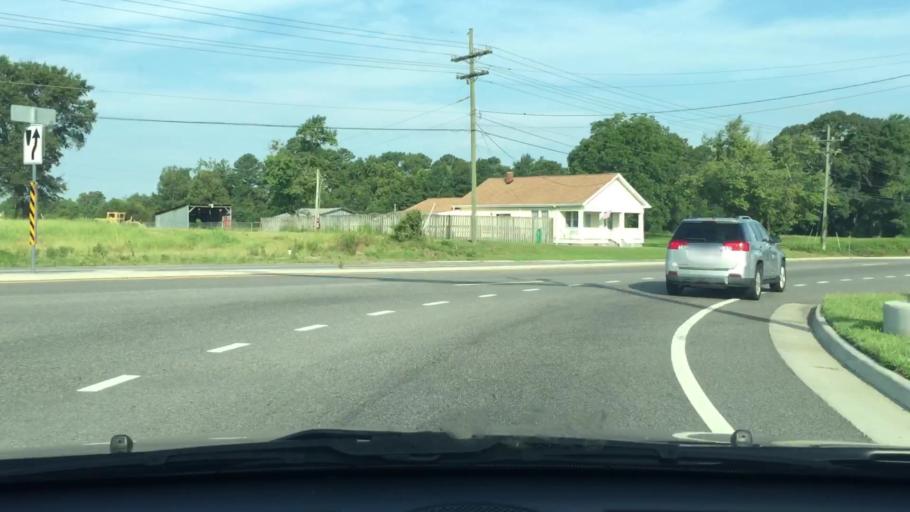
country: US
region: Virginia
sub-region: Isle of Wight County
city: Carrollton
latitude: 36.9382
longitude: -76.5865
